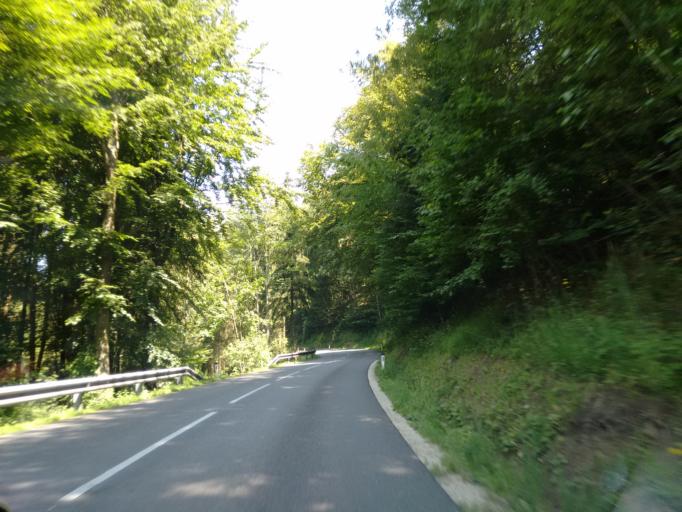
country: AT
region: Upper Austria
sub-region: Politischer Bezirk Urfahr-Umgebung
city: Altenberg bei Linz
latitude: 48.3638
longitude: 14.3334
